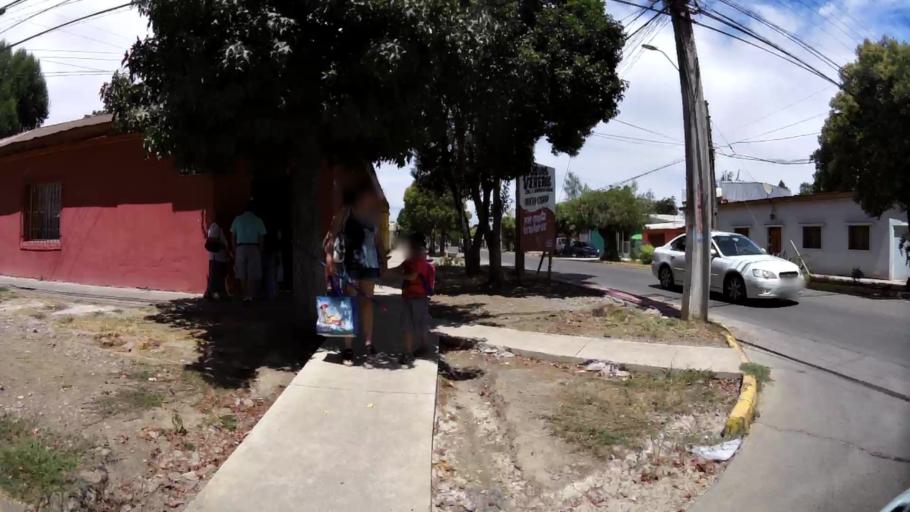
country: CL
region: O'Higgins
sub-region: Provincia de Cachapoal
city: Graneros
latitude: -34.0622
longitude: -70.7279
